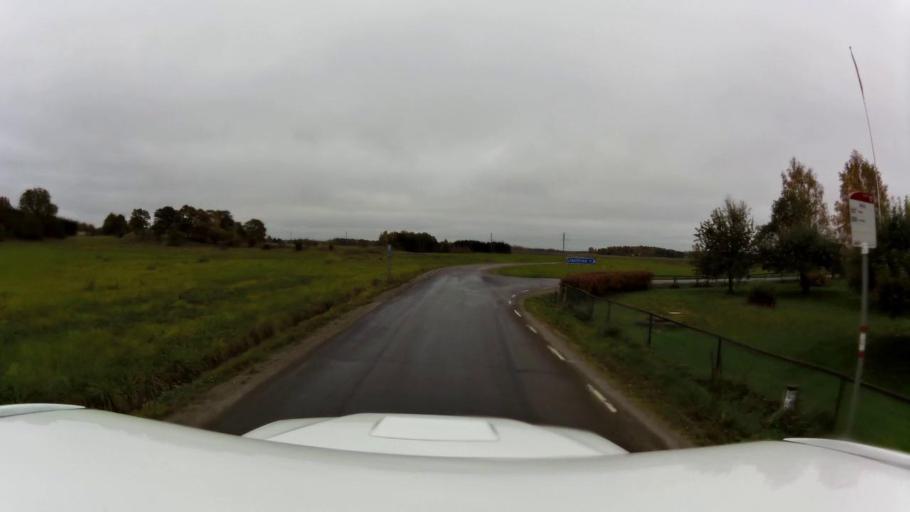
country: SE
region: OEstergoetland
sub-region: Linkopings Kommun
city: Ekangen
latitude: 58.4629
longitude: 15.7023
